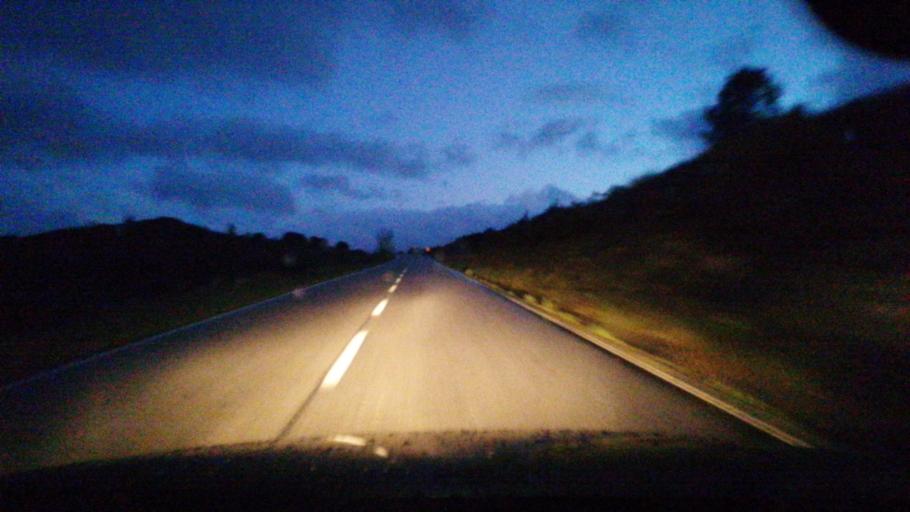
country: PT
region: Viseu
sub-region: Tabuaco
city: Tabuaco
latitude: 41.1380
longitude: -7.5233
